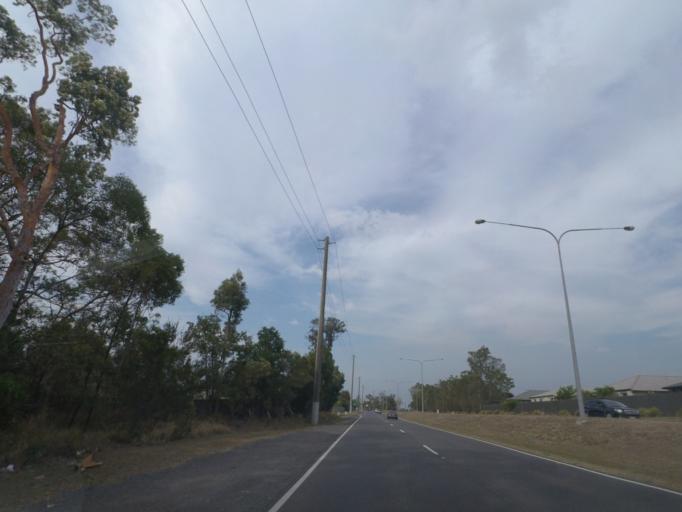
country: AU
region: Queensland
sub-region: Brisbane
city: Inala
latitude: -27.5954
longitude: 152.9892
